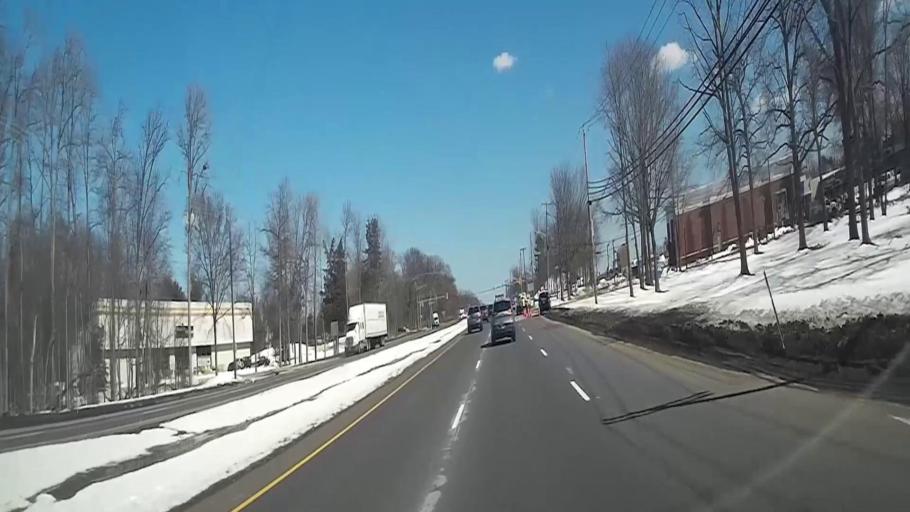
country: US
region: New Jersey
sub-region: Burlington County
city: Marlton
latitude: 39.8939
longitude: -74.9197
